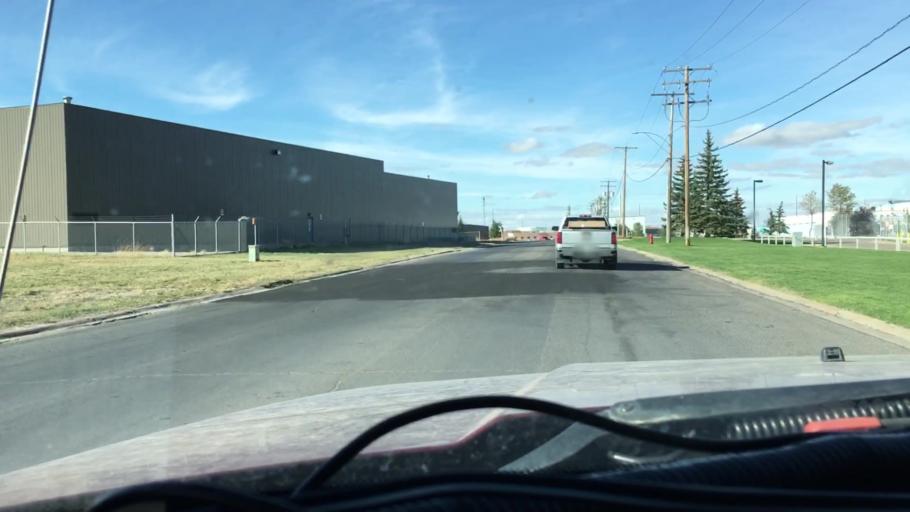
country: CA
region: Saskatchewan
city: Regina
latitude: 50.4755
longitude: -104.5615
